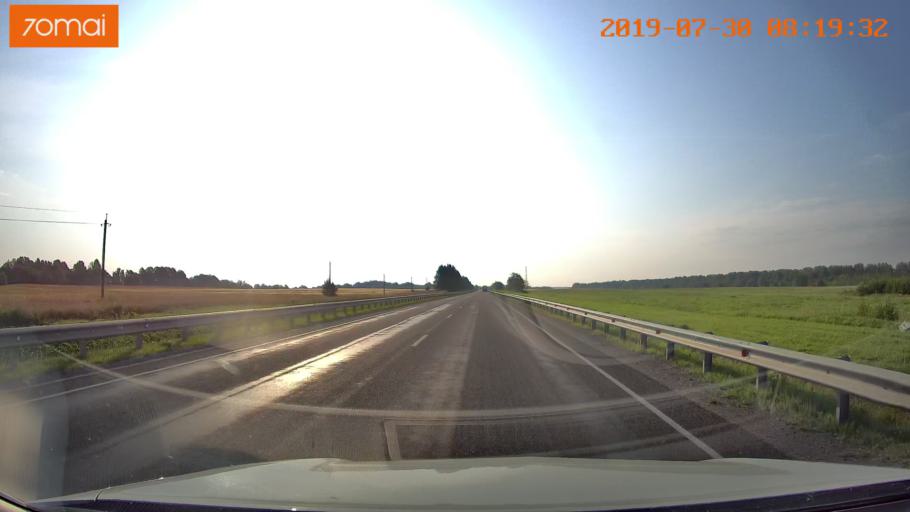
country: RU
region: Kaliningrad
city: Chernyakhovsk
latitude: 54.6281
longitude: 21.4941
